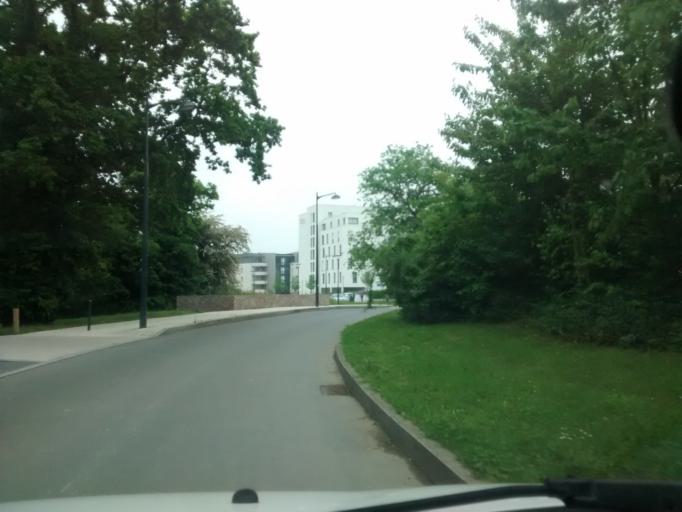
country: FR
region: Brittany
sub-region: Departement d'Ille-et-Vilaine
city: Saint-Gregoire
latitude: 48.1323
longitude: -1.6971
